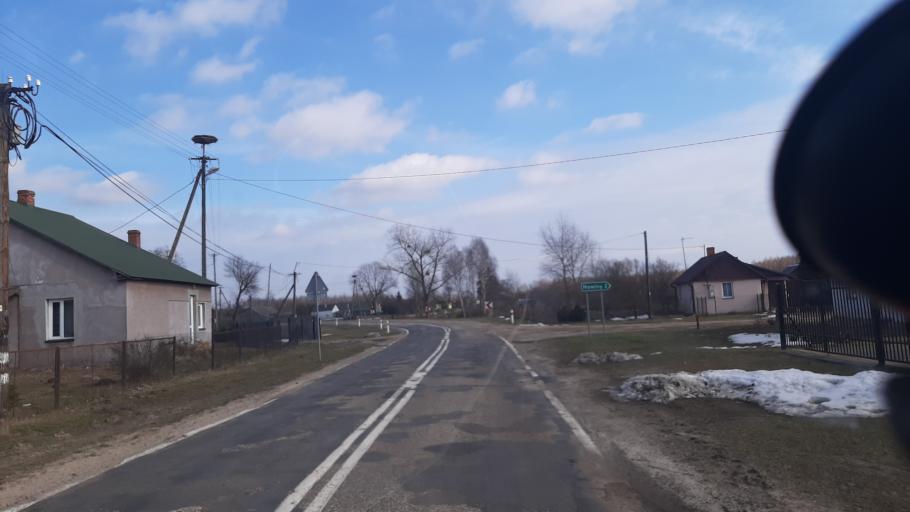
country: PL
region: Lublin Voivodeship
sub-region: Powiat wlodawski
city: Urszulin
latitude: 51.4932
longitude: 23.2345
